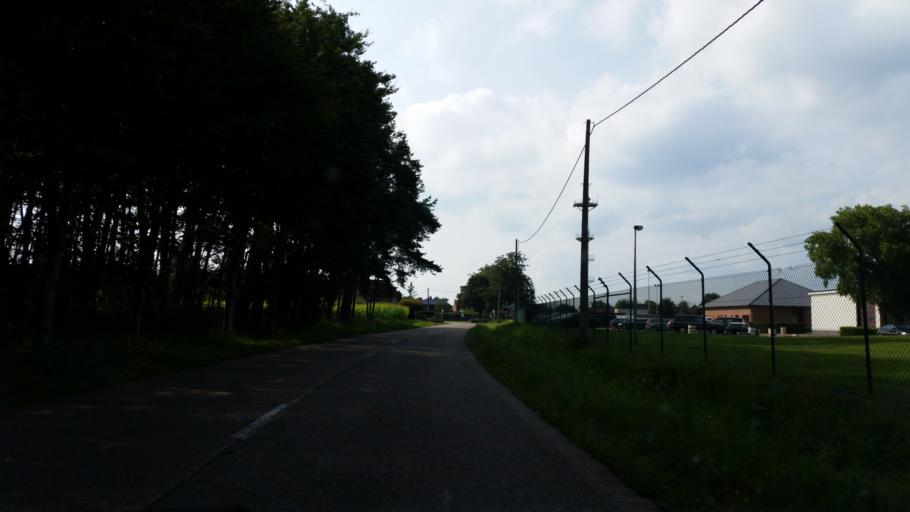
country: BE
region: Flanders
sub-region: Provincie Antwerpen
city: Kasterlee
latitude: 51.2447
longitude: 4.9120
